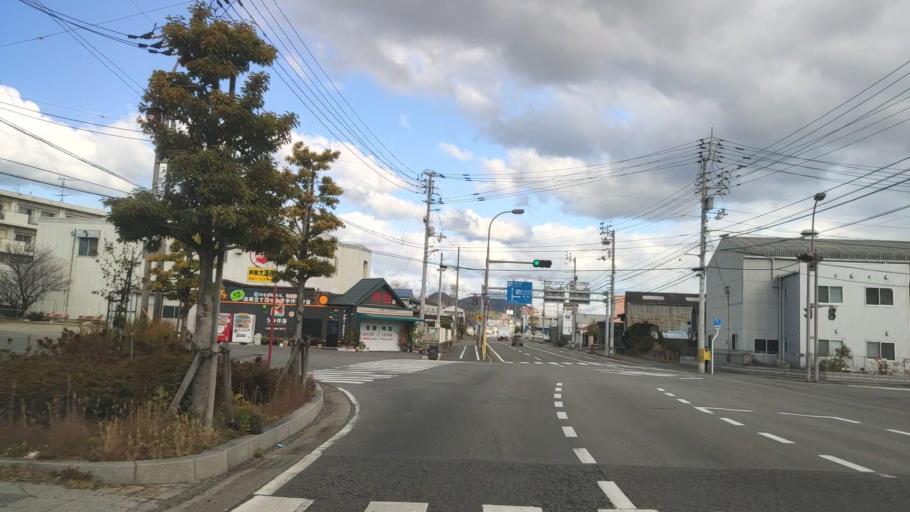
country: JP
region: Ehime
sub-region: Shikoku-chuo Shi
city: Matsuyama
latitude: 33.8532
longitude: 132.7130
